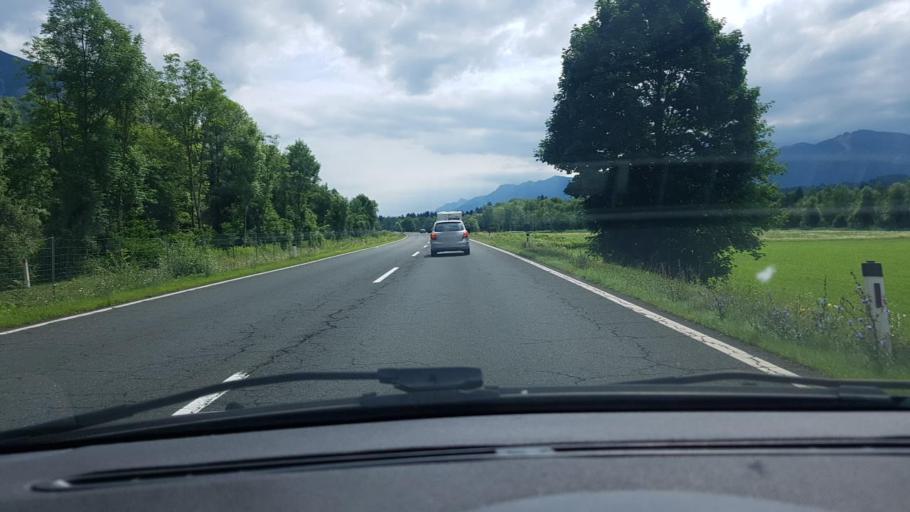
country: AT
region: Carinthia
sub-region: Politischer Bezirk Villach Land
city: Feistritz an der Gail
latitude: 46.5769
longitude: 13.6266
